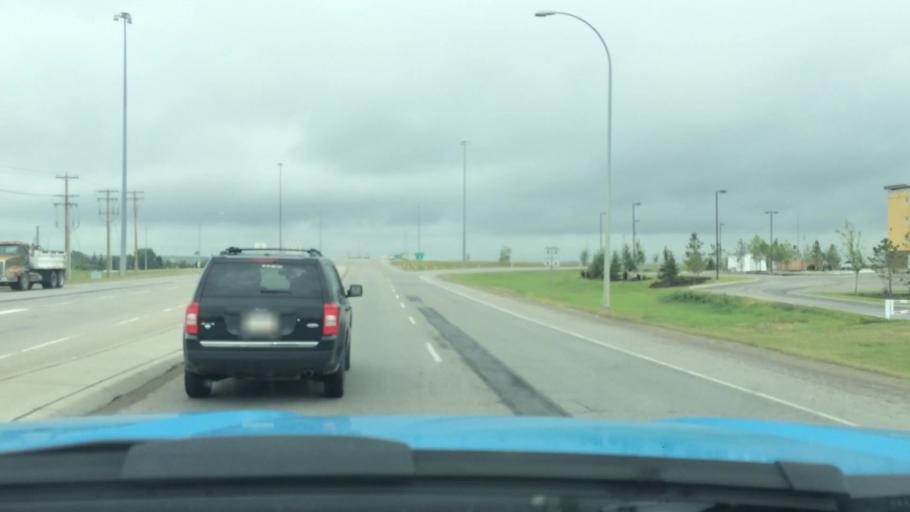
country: CA
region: Alberta
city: Airdrie
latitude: 51.3001
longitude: -113.9959
